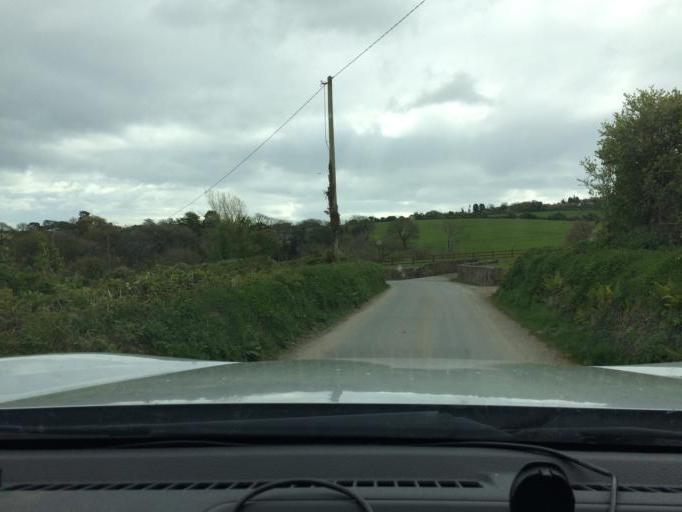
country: IE
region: Munster
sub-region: Waterford
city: Dungarvan
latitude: 52.0547
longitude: -7.6265
